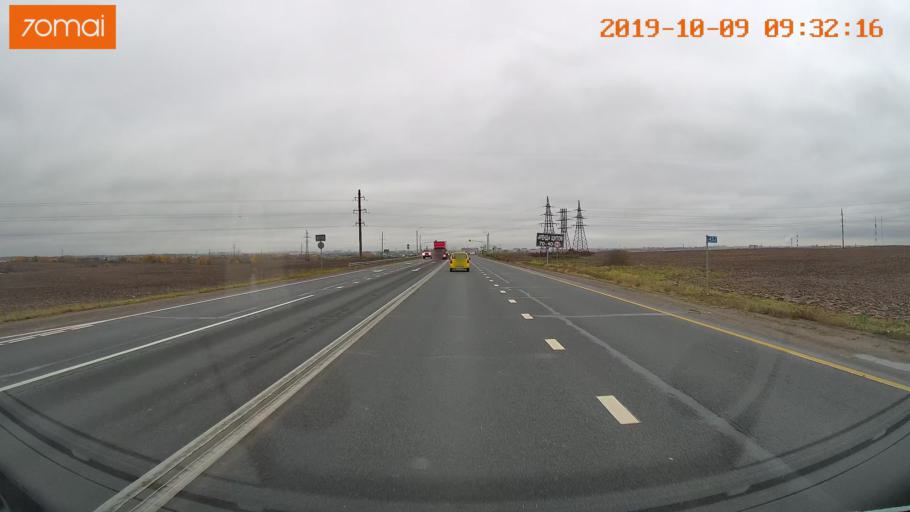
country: RU
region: Vologda
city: Vologda
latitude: 59.1570
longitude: 39.9304
